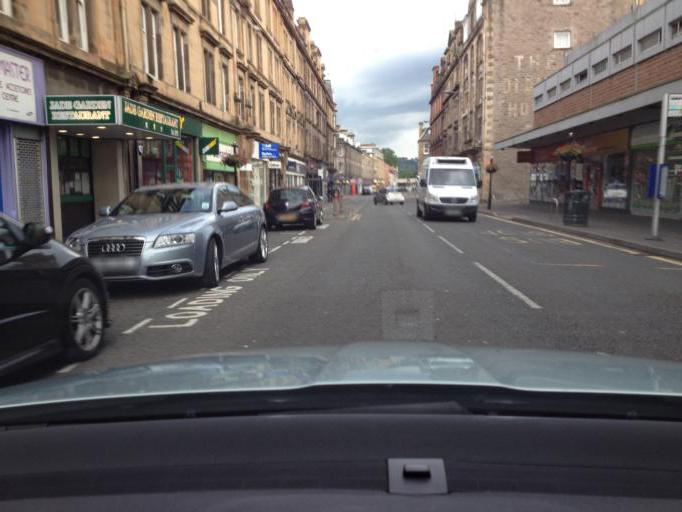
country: GB
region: Scotland
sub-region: Perth and Kinross
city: Perth
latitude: 56.3963
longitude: -3.4324
